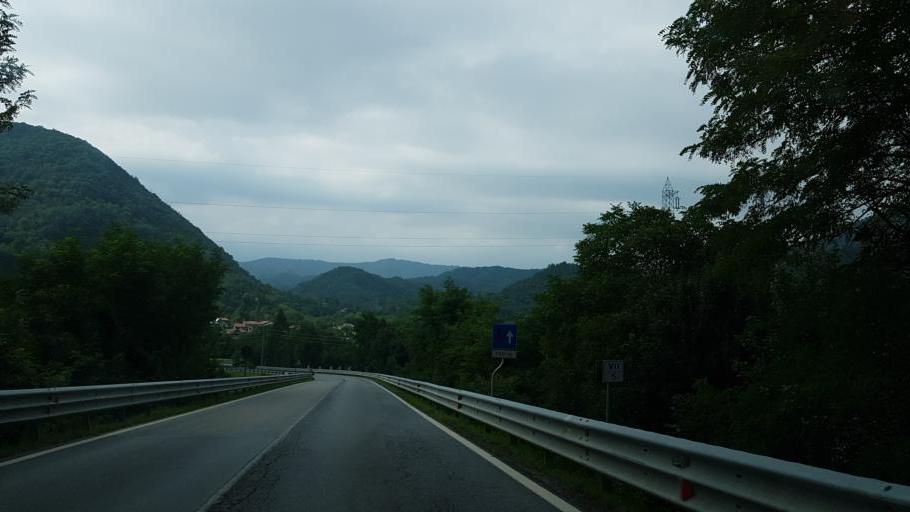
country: IT
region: Piedmont
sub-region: Provincia di Cuneo
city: Gaiola
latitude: 44.3350
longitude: 7.4191
